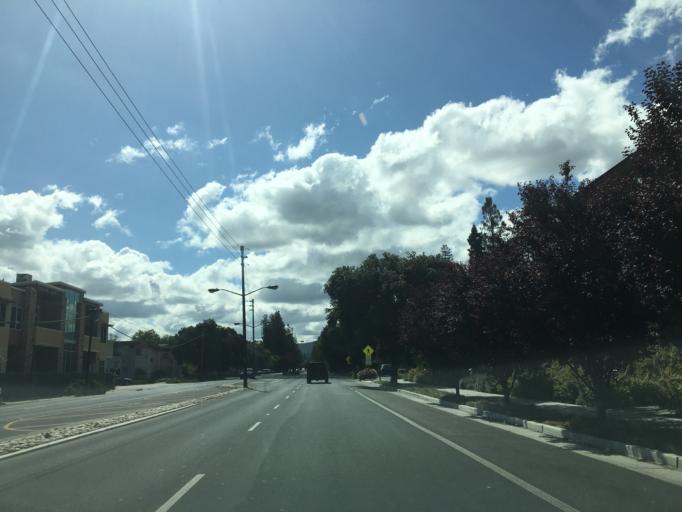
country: US
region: California
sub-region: Santa Clara County
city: Los Altos
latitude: 37.3995
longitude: -122.1144
